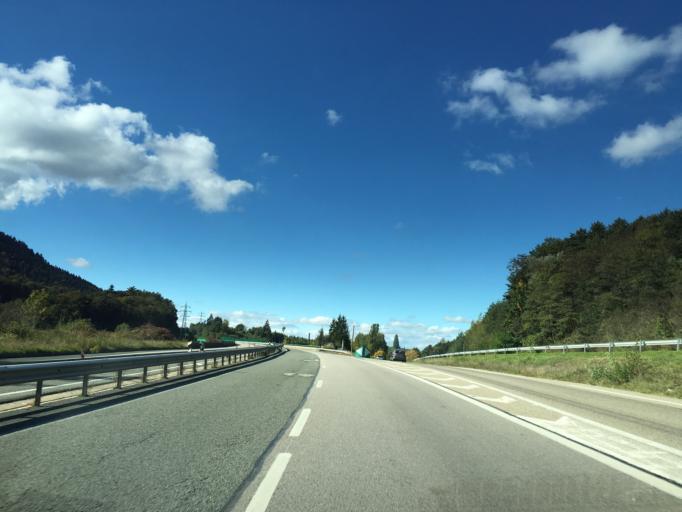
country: FR
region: Lorraine
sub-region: Departement des Vosges
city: Etival-Clairefontaine
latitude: 48.3915
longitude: 6.8618
